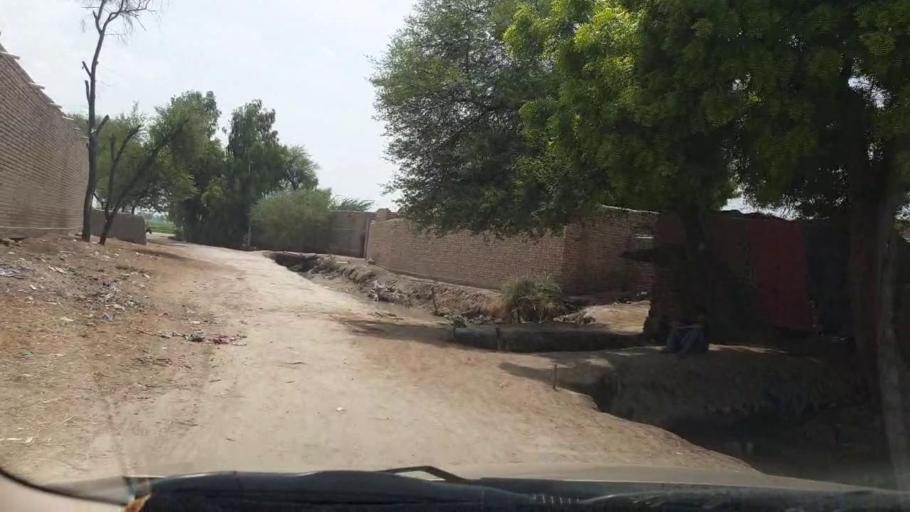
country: PK
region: Sindh
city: Larkana
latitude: 27.6248
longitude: 68.1512
